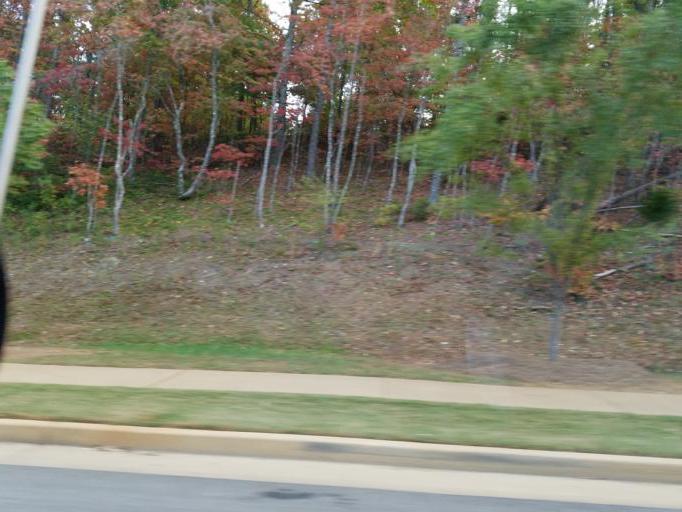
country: US
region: Georgia
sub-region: Bartow County
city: Cartersville
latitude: 34.1751
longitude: -84.7702
